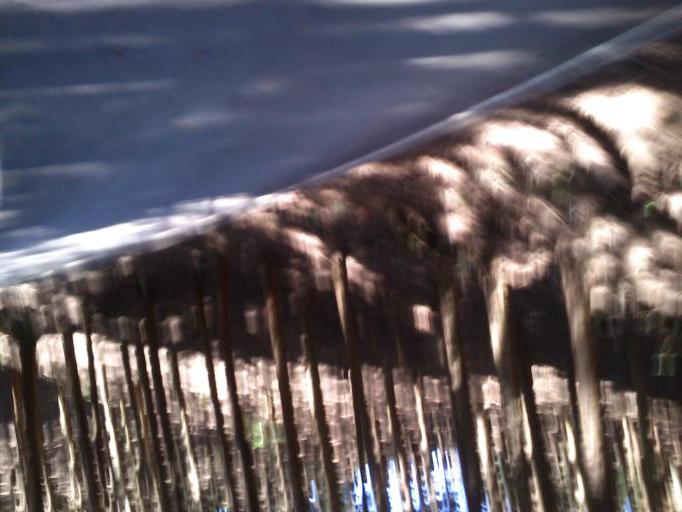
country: JP
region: Kyoto
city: Uji
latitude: 34.8486
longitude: 135.9463
